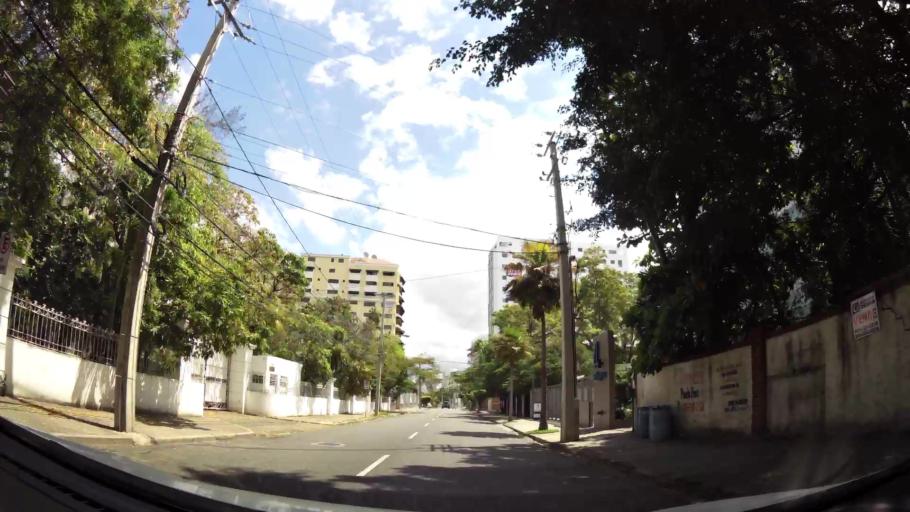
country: DO
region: Nacional
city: La Julia
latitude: 18.4723
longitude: -69.9290
